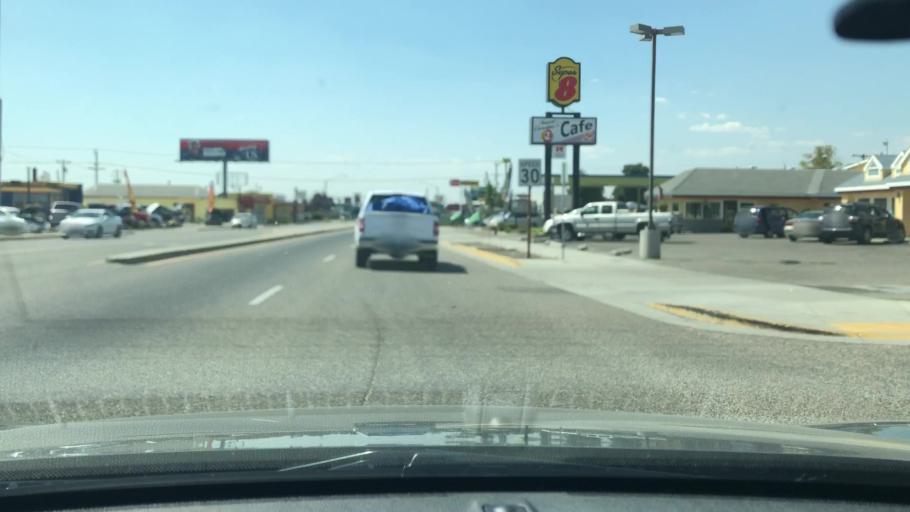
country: US
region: Oregon
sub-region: Malheur County
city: Ontario
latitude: 44.0251
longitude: -116.9531
